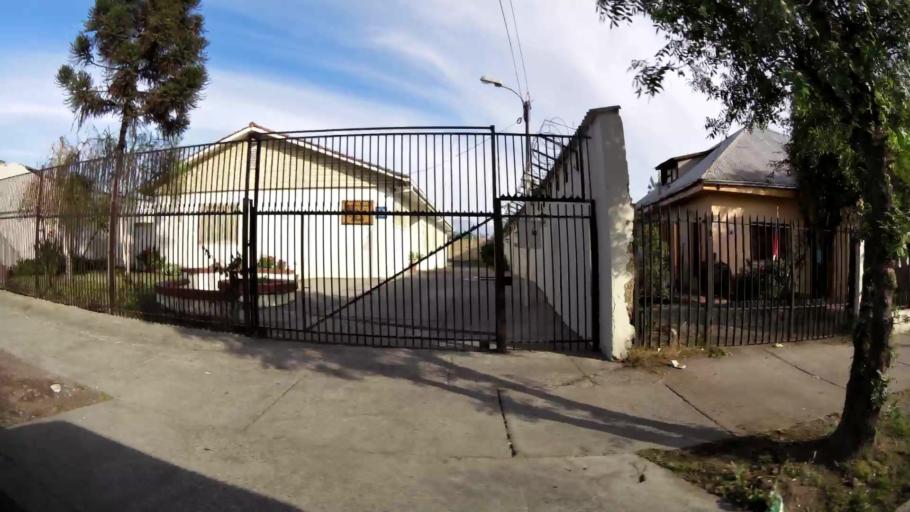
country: CL
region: Santiago Metropolitan
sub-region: Provincia de Cordillera
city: Puente Alto
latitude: -33.6138
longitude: -70.5863
